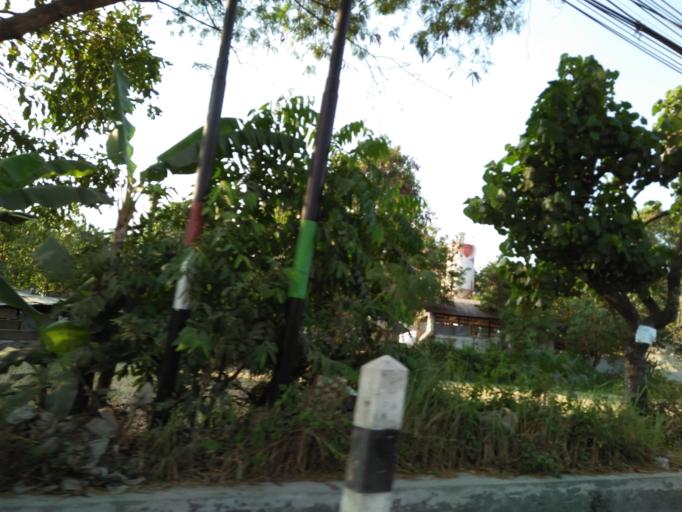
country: ID
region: Daerah Istimewa Yogyakarta
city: Depok
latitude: -7.7768
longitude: 110.4595
